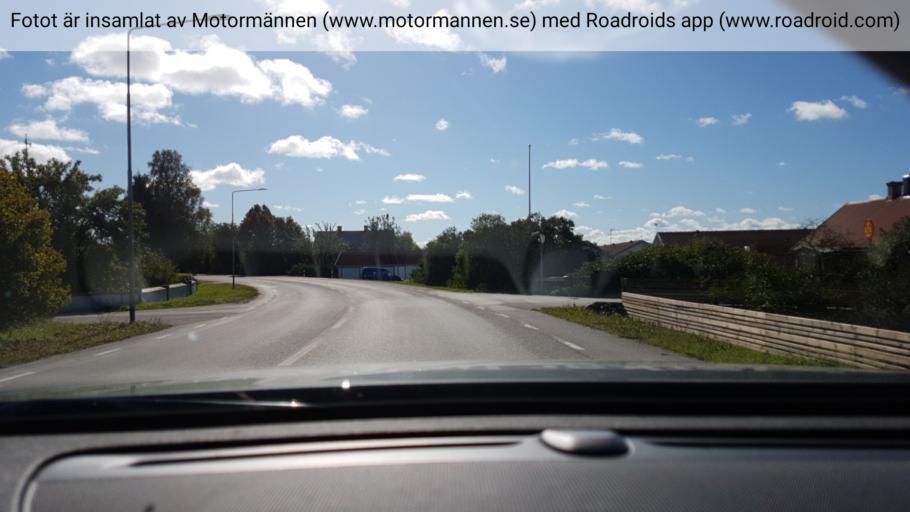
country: SE
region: Gotland
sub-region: Gotland
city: Slite
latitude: 57.7238
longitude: 18.7884
